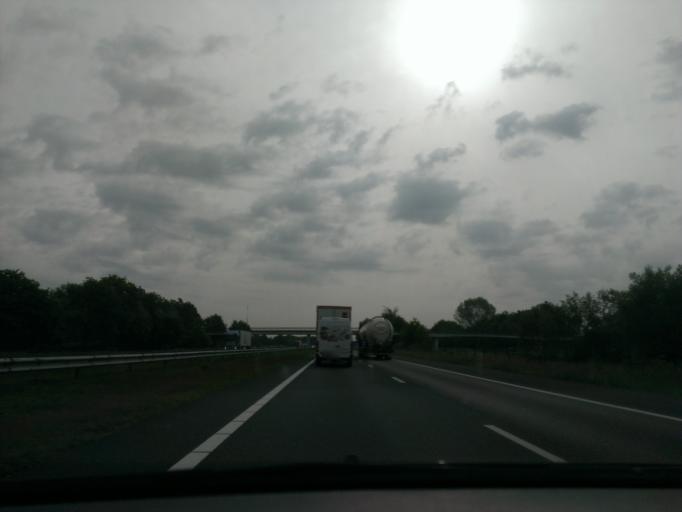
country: NL
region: Gelderland
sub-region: Gemeente Lochem
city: Laren
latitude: 52.2450
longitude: 6.3451
